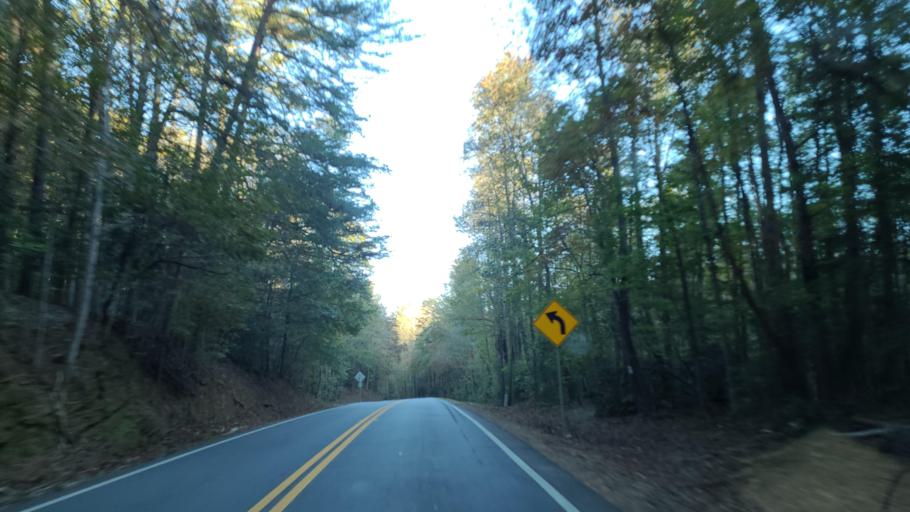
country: US
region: Georgia
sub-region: Lumpkin County
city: Dahlonega
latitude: 34.6271
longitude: -83.9490
